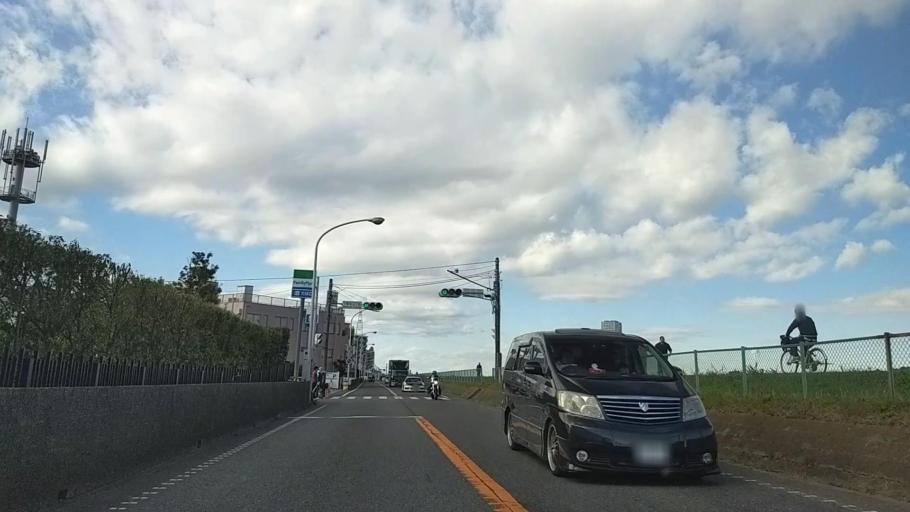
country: JP
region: Tokyo
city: Tokyo
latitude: 35.5967
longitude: 139.6409
